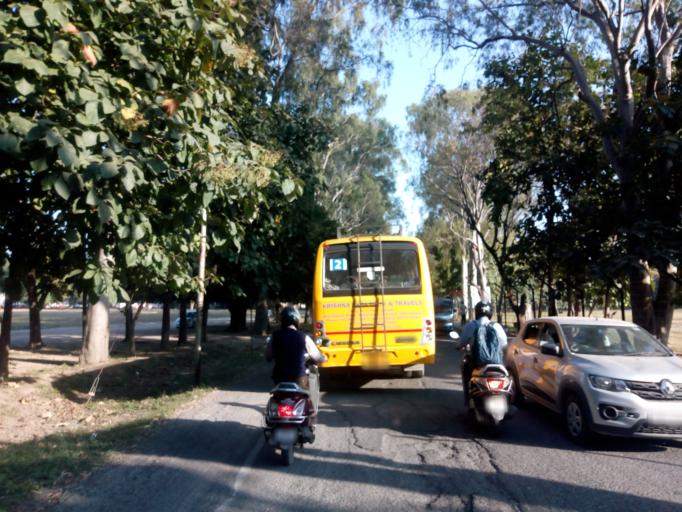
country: IN
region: Uttarakhand
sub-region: Dehradun
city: Dehradun
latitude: 30.3521
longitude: 78.0324
